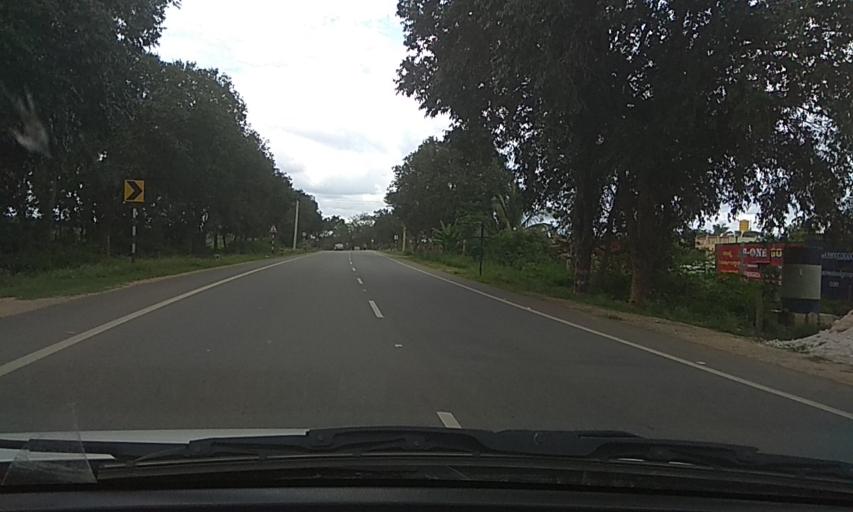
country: IN
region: Karnataka
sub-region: Tumkur
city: Tumkur
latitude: 13.2599
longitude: 77.0880
